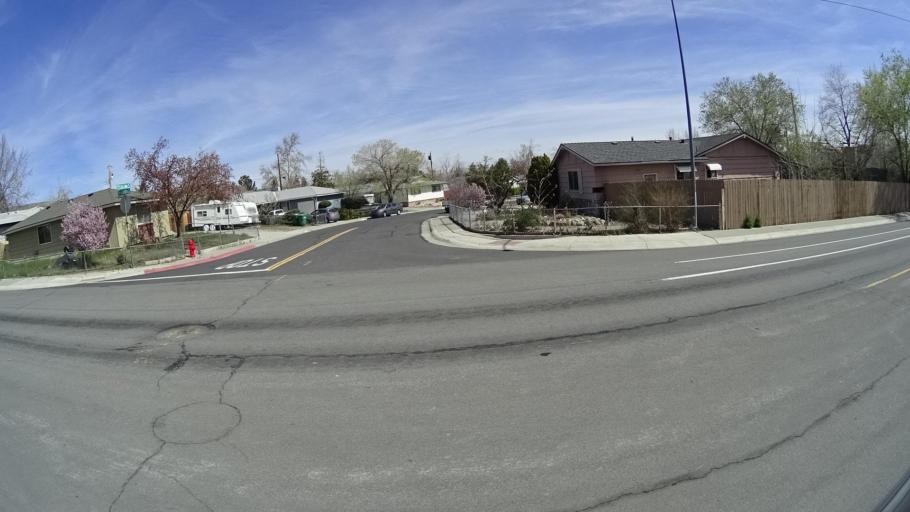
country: US
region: Nevada
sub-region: Washoe County
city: Reno
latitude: 39.5316
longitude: -119.8572
